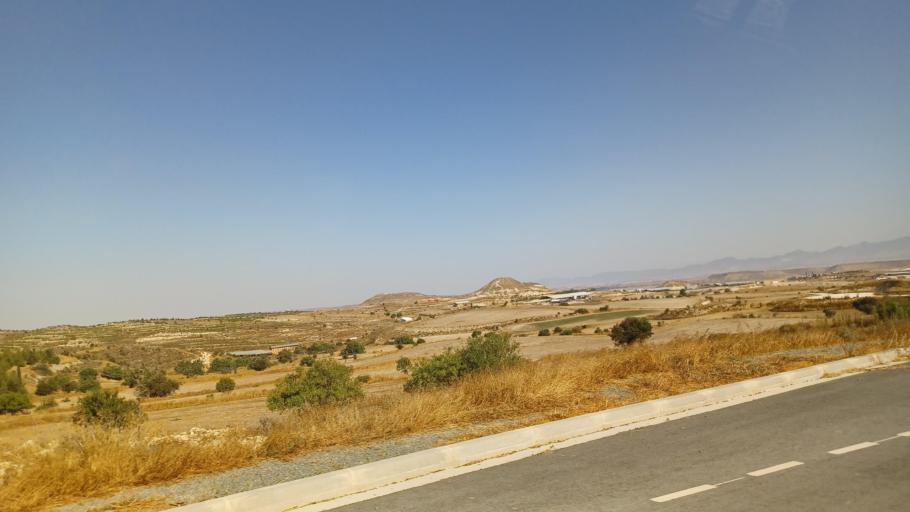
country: CY
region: Larnaka
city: Athienou
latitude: 35.0257
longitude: 33.5474
